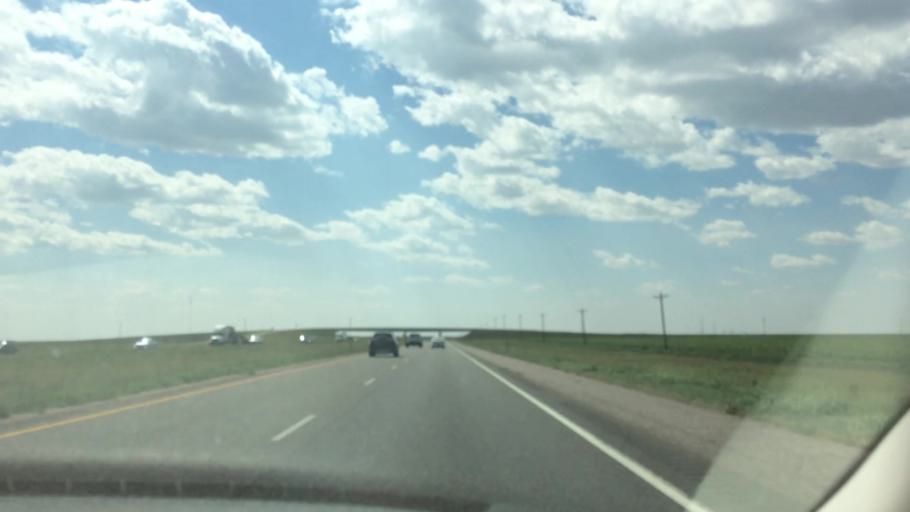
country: US
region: Colorado
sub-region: Lincoln County
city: Hugo
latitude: 39.2877
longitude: -103.0930
